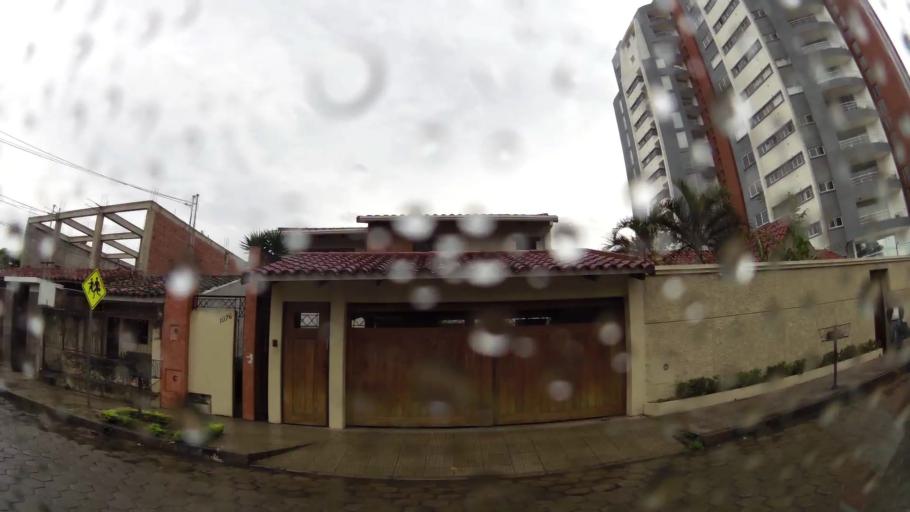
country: BO
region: Santa Cruz
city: Santa Cruz de la Sierra
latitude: -17.7789
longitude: -63.1688
